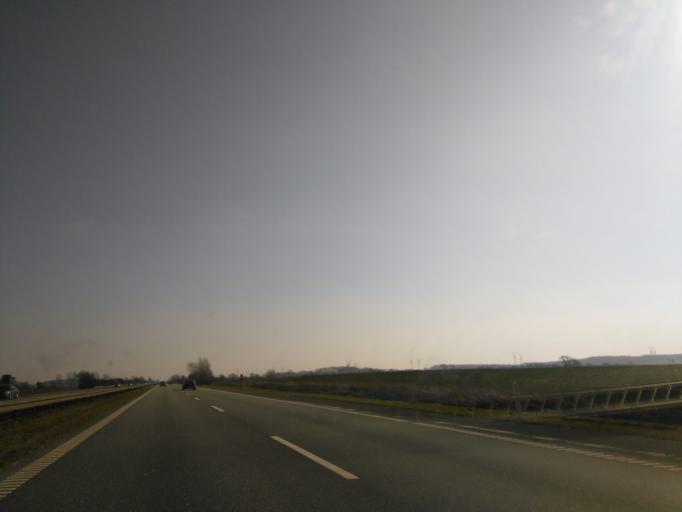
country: DK
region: South Denmark
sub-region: Assens Kommune
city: Arup
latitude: 55.4238
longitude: 10.0092
